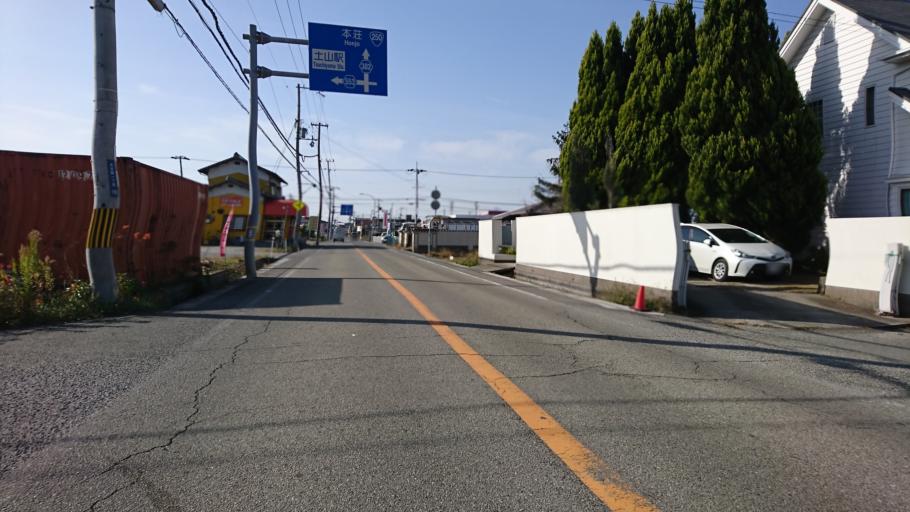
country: JP
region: Hyogo
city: Kakogawacho-honmachi
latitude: 34.7267
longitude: 134.8676
